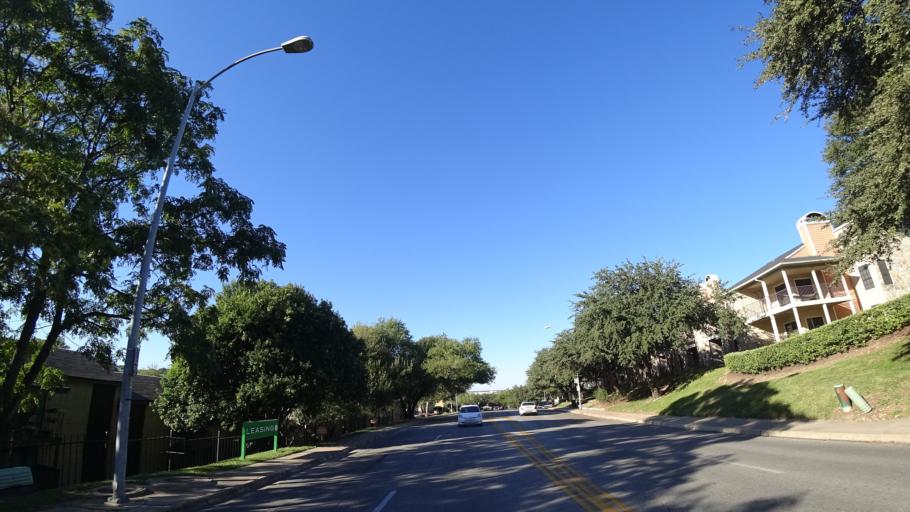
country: US
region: Texas
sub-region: Travis County
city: Austin
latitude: 30.2288
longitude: -97.7215
